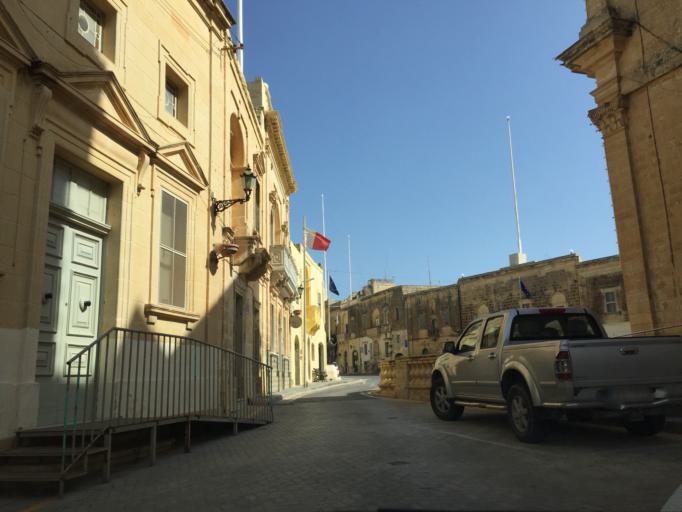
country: MT
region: L-Gharb
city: Gharb
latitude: 36.0602
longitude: 14.2091
